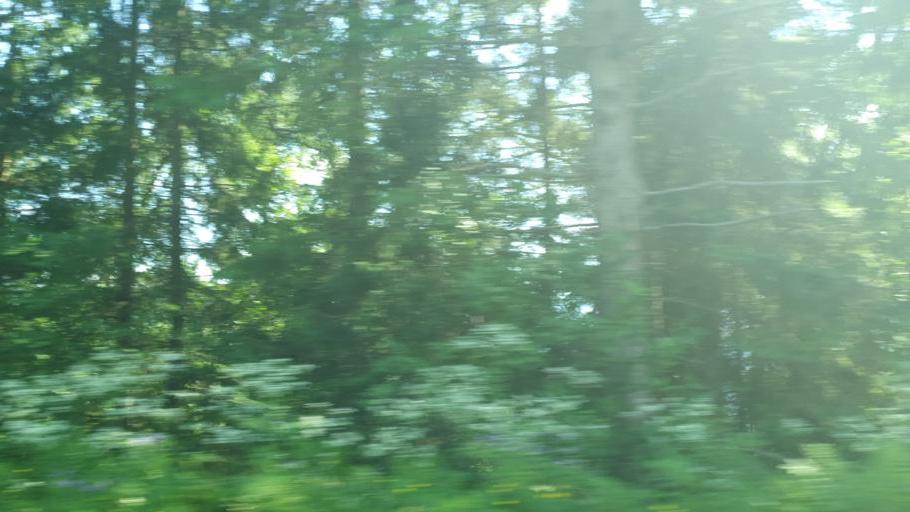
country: NO
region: Nord-Trondelag
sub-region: Leksvik
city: Leksvik
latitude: 63.6939
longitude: 10.7025
